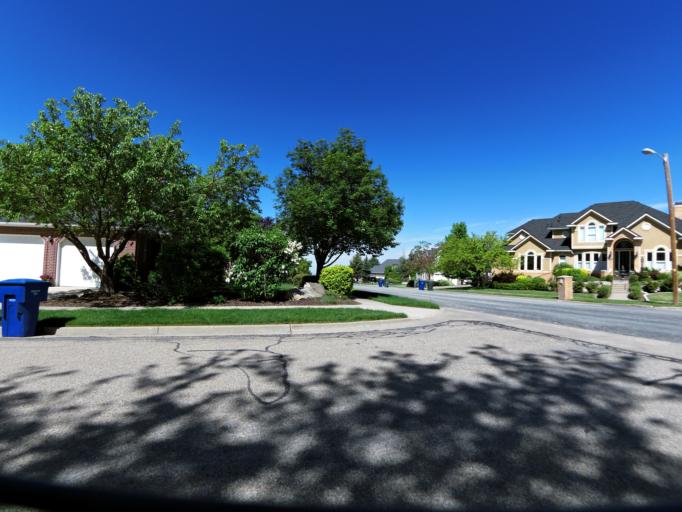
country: US
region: Utah
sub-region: Weber County
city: Uintah
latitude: 41.1728
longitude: -111.9340
